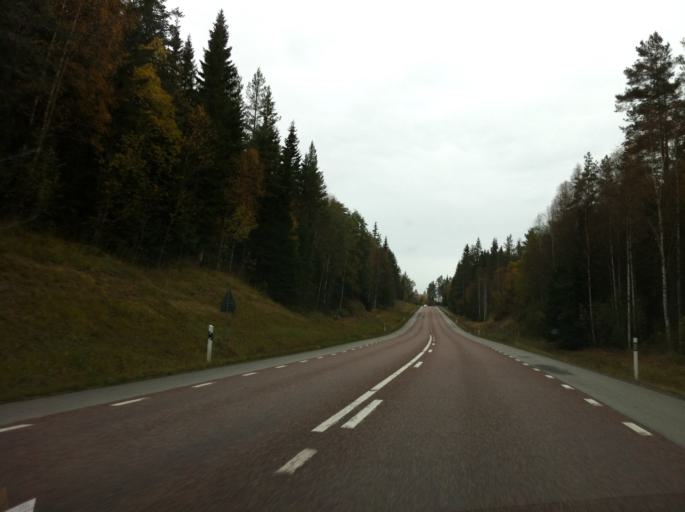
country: SE
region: Dalarna
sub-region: Ludvika Kommun
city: Grangesberg
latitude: 59.9918
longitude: 15.0176
